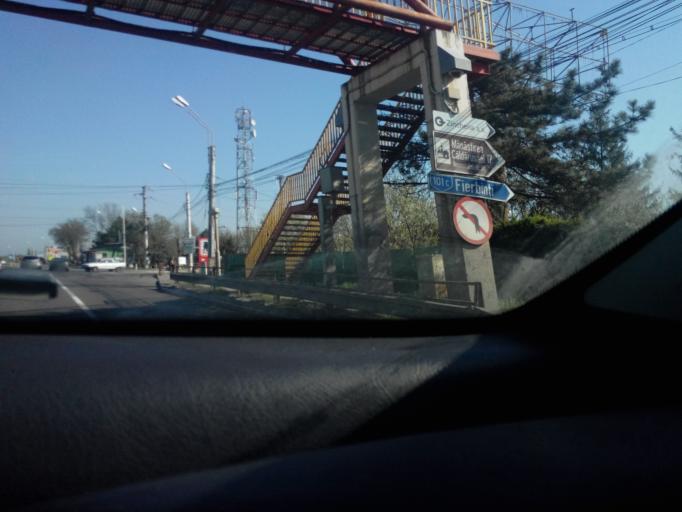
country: RO
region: Ilfov
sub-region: Comuna Corbeanca
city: Corbeanca
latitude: 44.6086
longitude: 26.0723
